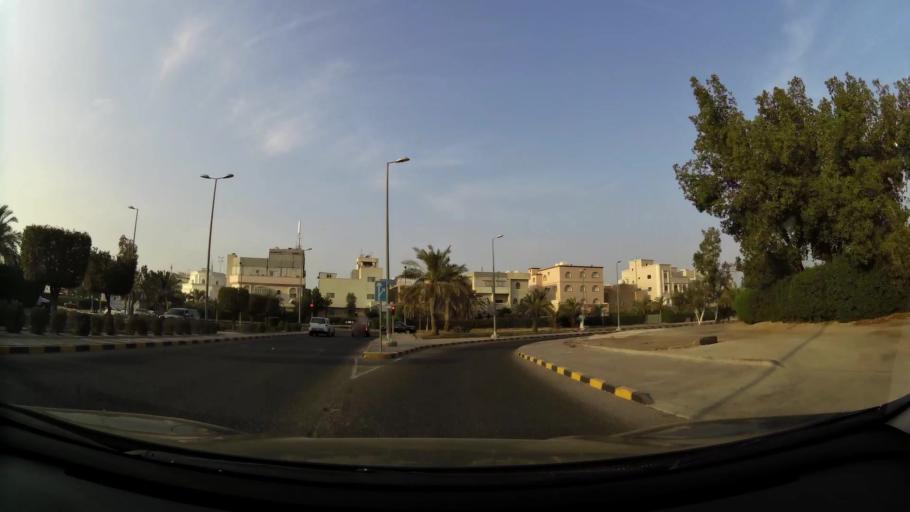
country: KW
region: Mubarak al Kabir
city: Sabah as Salim
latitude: 29.2573
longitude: 48.0700
